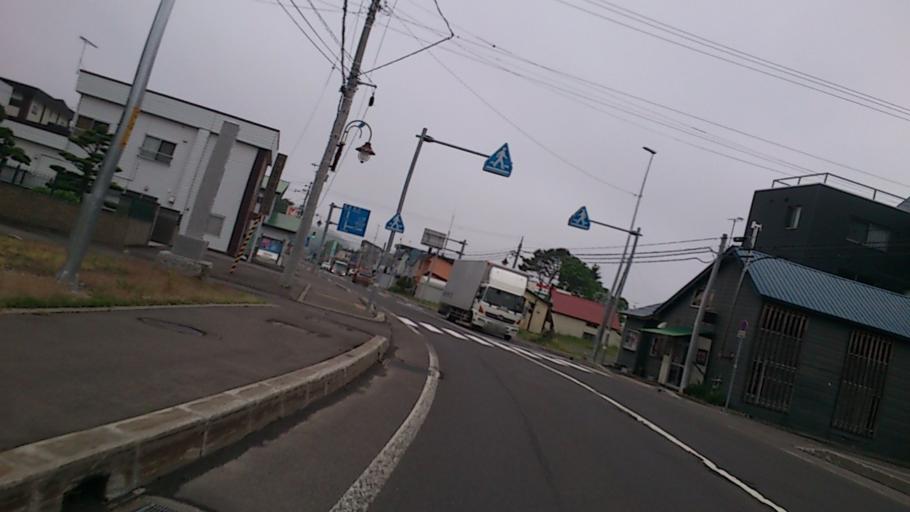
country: JP
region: Hokkaido
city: Niseko Town
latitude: 42.8588
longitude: 140.8877
